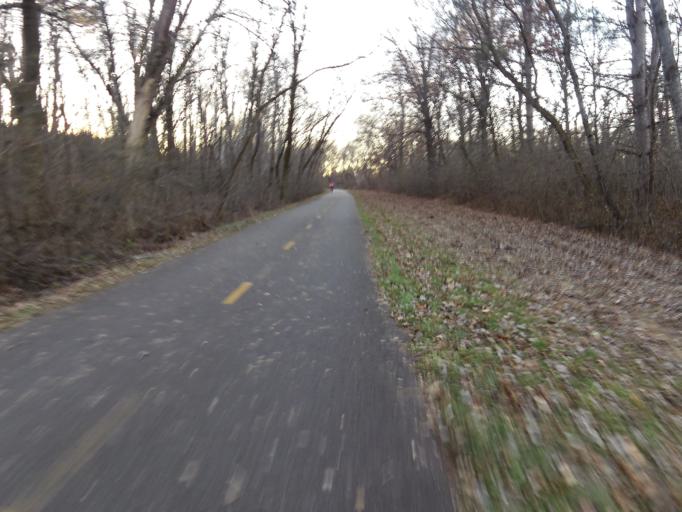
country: US
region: Minnesota
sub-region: Washington County
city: Grant
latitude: 45.0916
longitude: -92.8864
